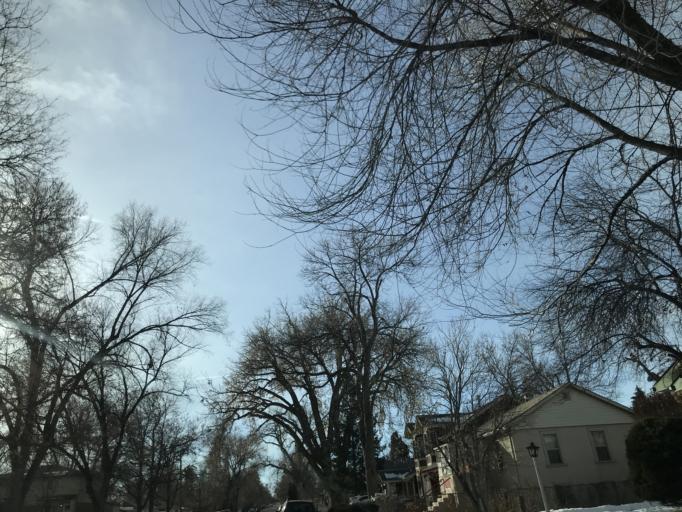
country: US
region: Colorado
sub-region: Arapahoe County
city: Littleton
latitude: 39.6068
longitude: -105.0116
